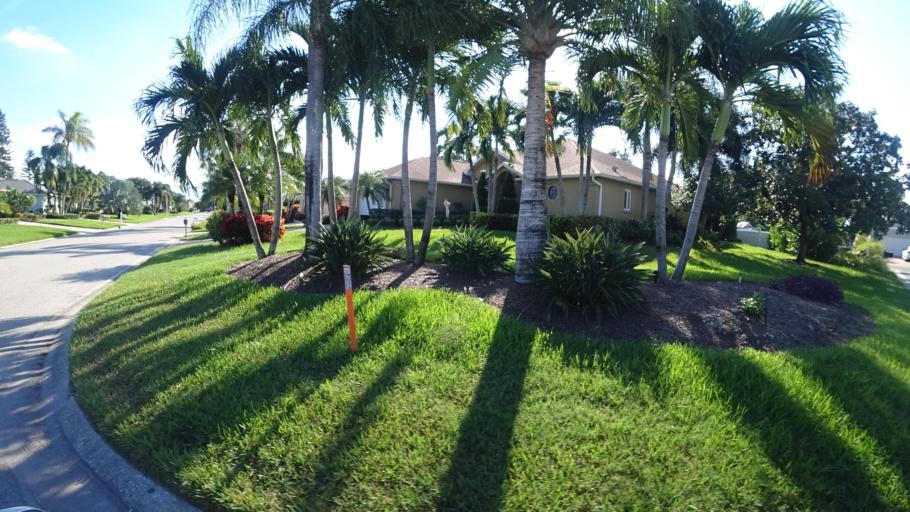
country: US
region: Florida
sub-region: Manatee County
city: Cortez
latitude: 27.4544
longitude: -82.6512
